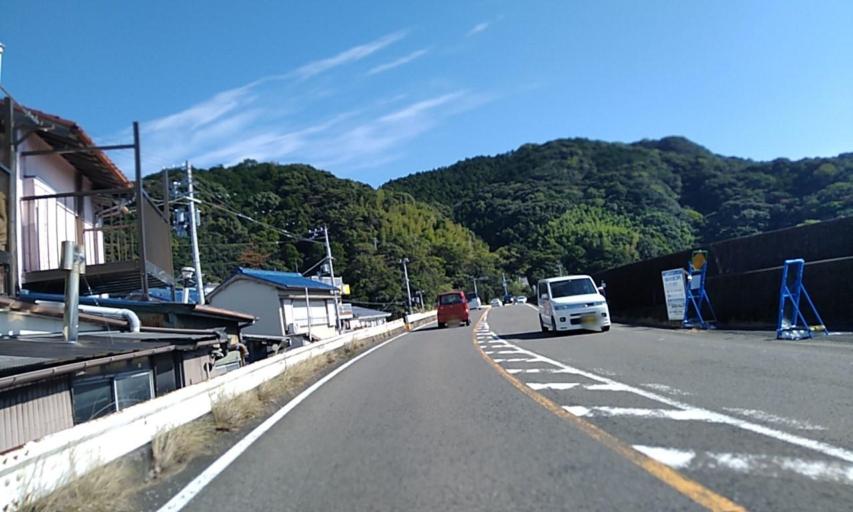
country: JP
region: Mie
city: Owase
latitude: 33.8912
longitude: 136.1066
